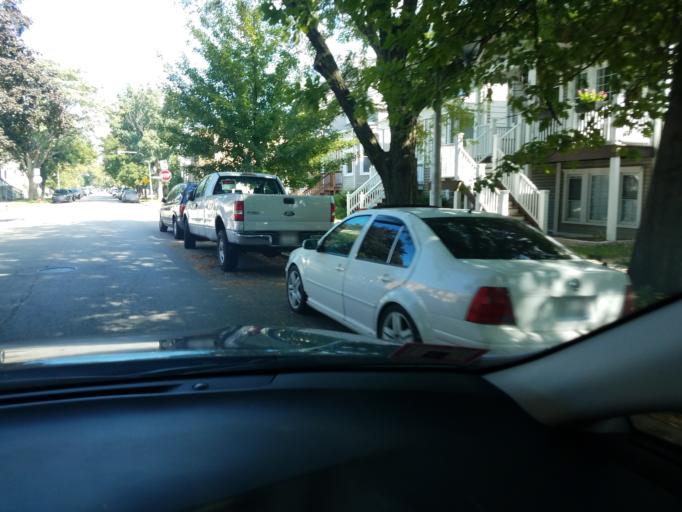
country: US
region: Illinois
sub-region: Cook County
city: Lincolnwood
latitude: 41.9479
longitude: -87.7030
